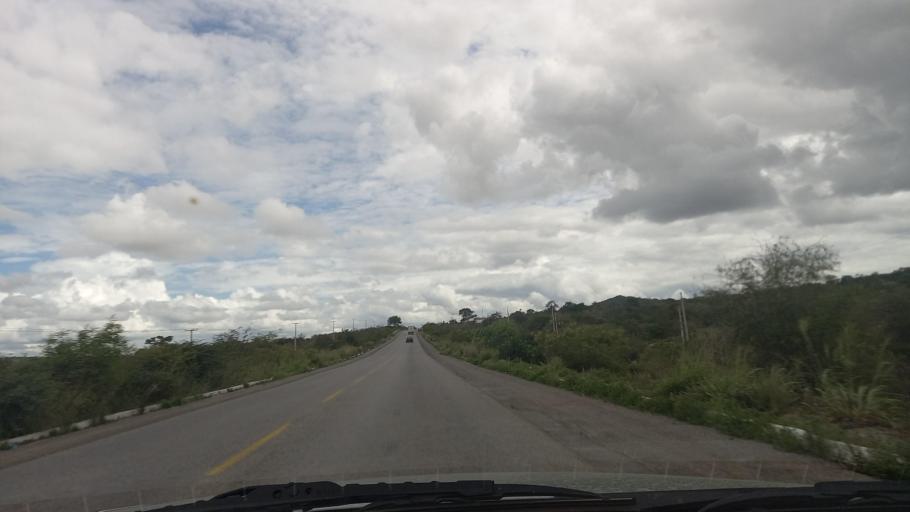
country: BR
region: Pernambuco
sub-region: Cachoeirinha
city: Cachoeirinha
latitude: -8.3411
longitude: -36.1607
